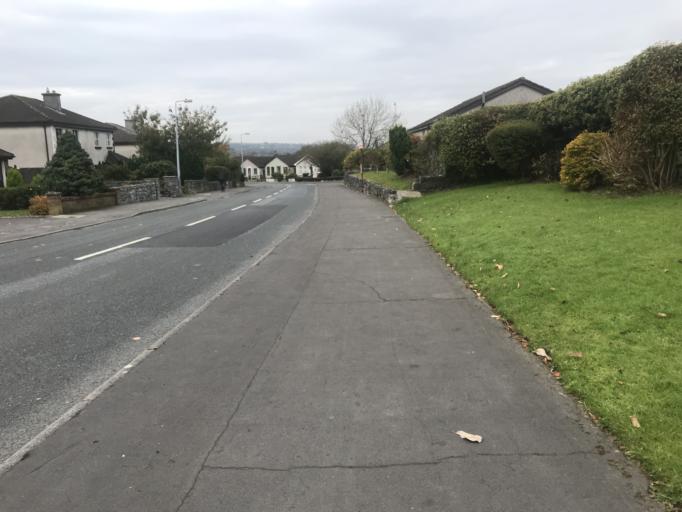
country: IE
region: Connaught
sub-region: County Galway
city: Gaillimh
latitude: 53.2925
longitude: -9.0494
